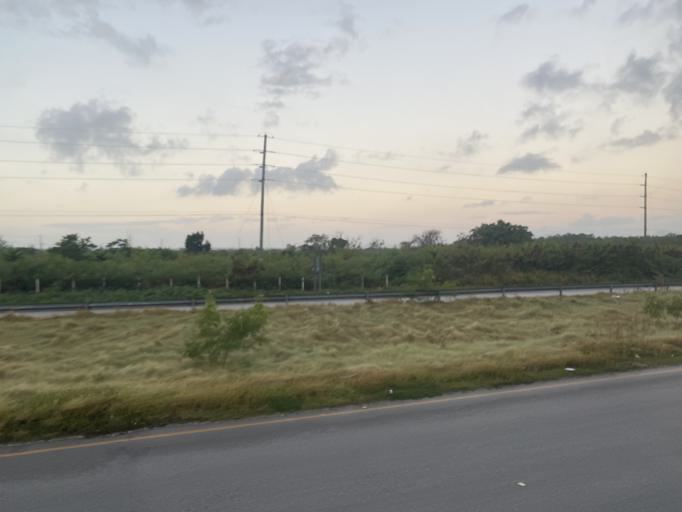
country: DO
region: San Juan
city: Punta Cana
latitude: 18.7020
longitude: -68.4630
